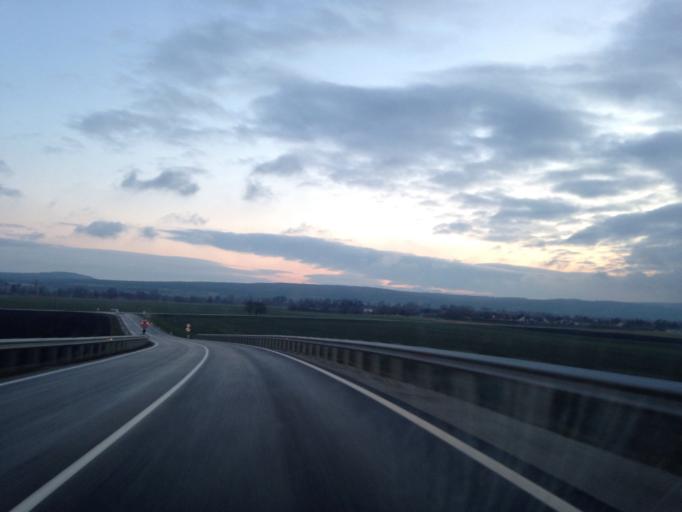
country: AT
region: Lower Austria
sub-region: Politischer Bezirk Bruck an der Leitha
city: Bruck an der Leitha
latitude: 48.0207
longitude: 16.7403
